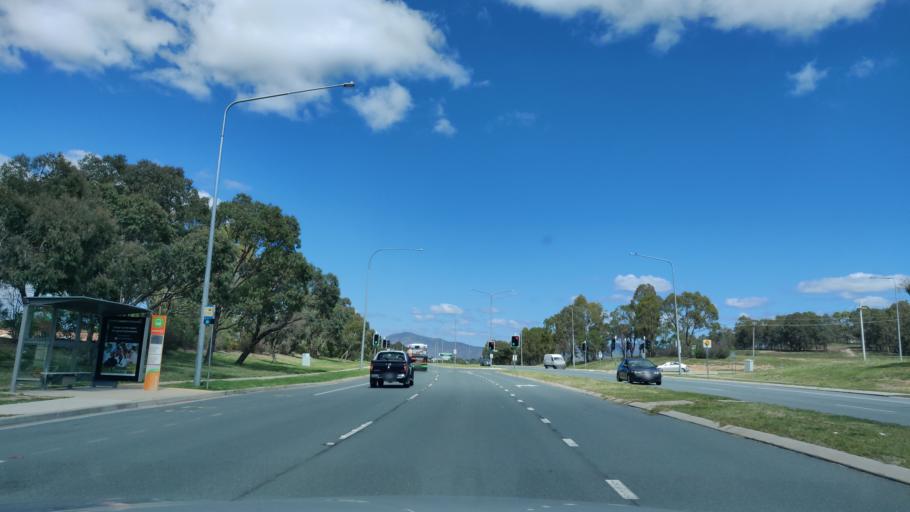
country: AU
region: Australian Capital Territory
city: Macarthur
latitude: -35.4026
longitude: 149.0650
